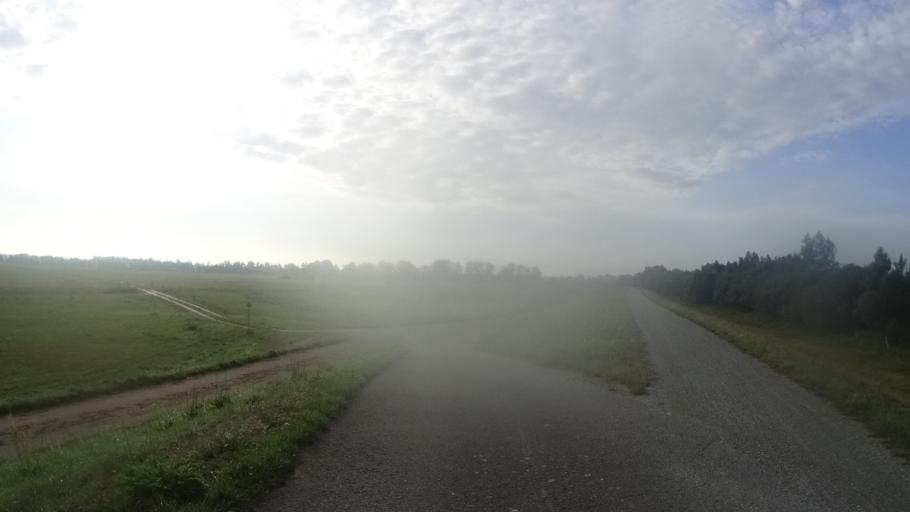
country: DE
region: Brandenburg
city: Lanz
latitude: 53.0501
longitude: 11.5696
